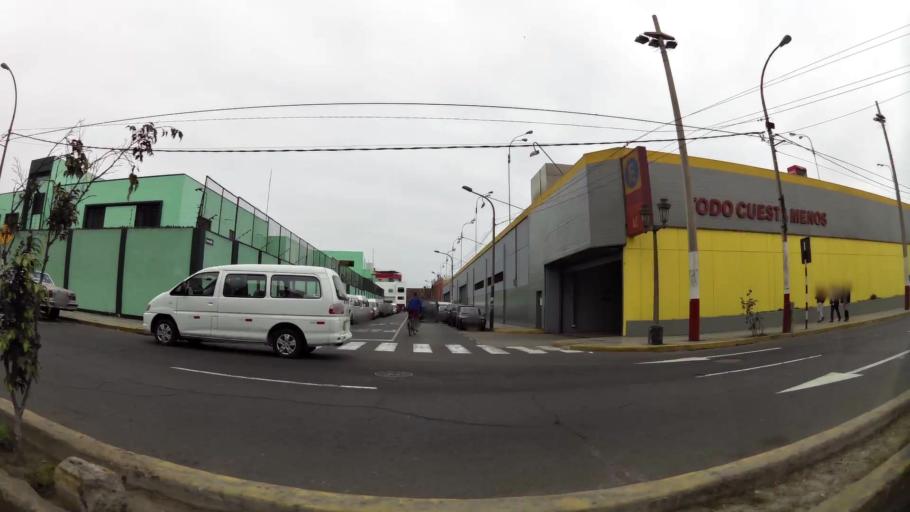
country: PE
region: Callao
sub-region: Callao
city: Callao
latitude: -12.0598
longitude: -77.1312
